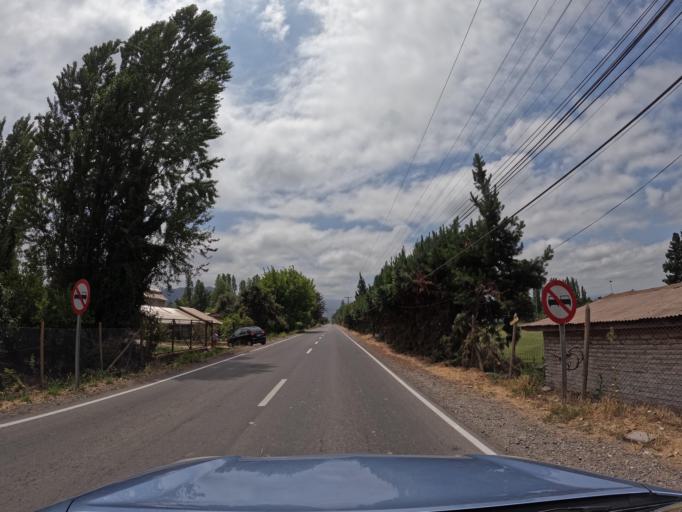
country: CL
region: O'Higgins
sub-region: Provincia de Colchagua
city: Chimbarongo
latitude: -34.7330
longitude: -70.9837
